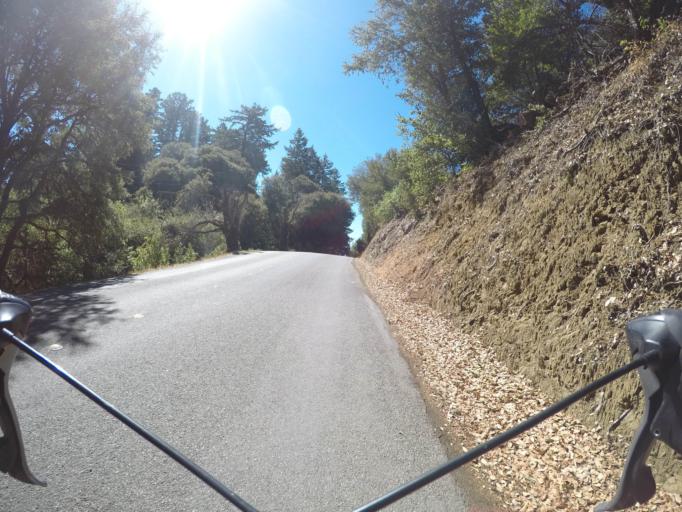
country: US
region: California
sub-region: San Mateo County
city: Portola Valley
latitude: 37.3137
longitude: -122.1971
